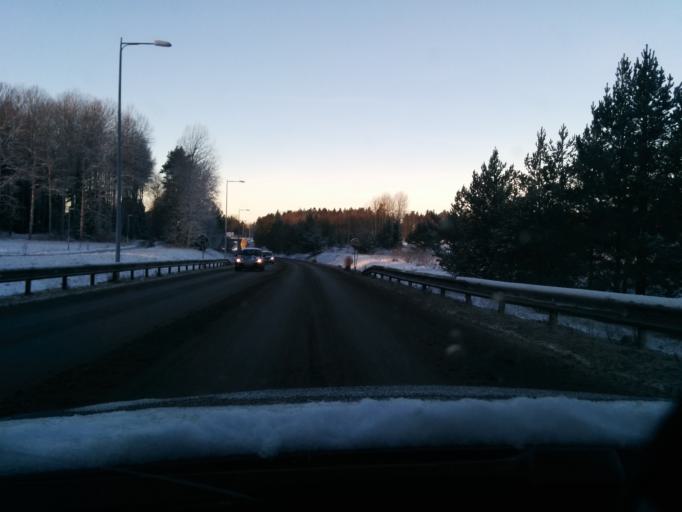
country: SE
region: Stockholm
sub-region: Taby Kommun
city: Taby
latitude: 59.4647
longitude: 18.0691
